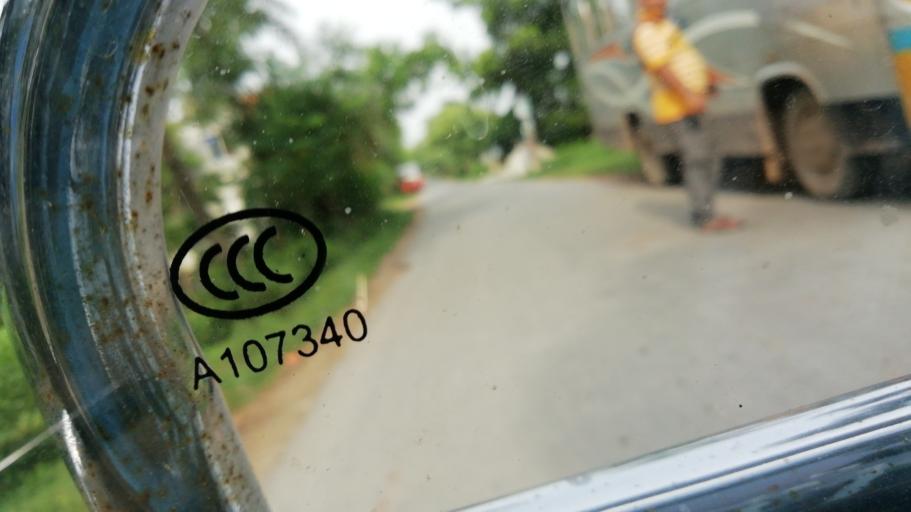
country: BD
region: Khulna
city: Kesabpur
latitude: 23.0310
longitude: 89.2728
